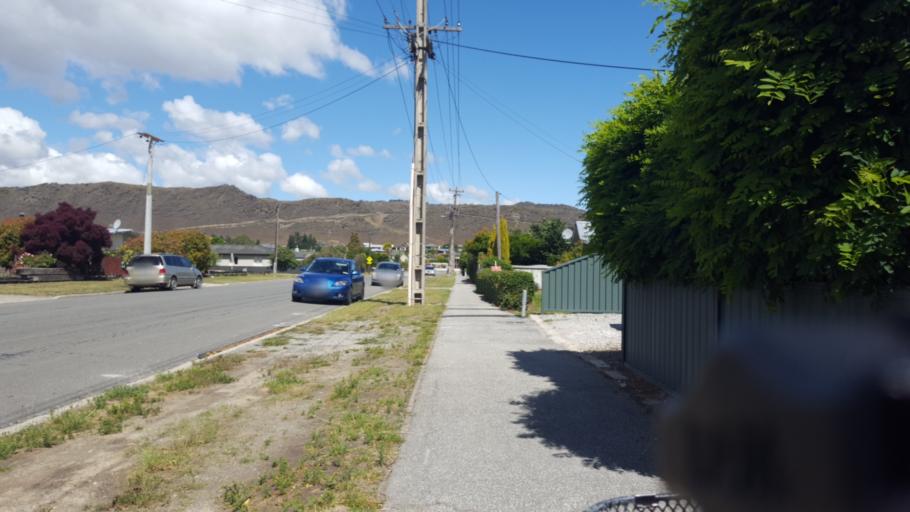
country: NZ
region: Otago
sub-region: Queenstown-Lakes District
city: Wanaka
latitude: -45.2473
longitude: 169.3948
